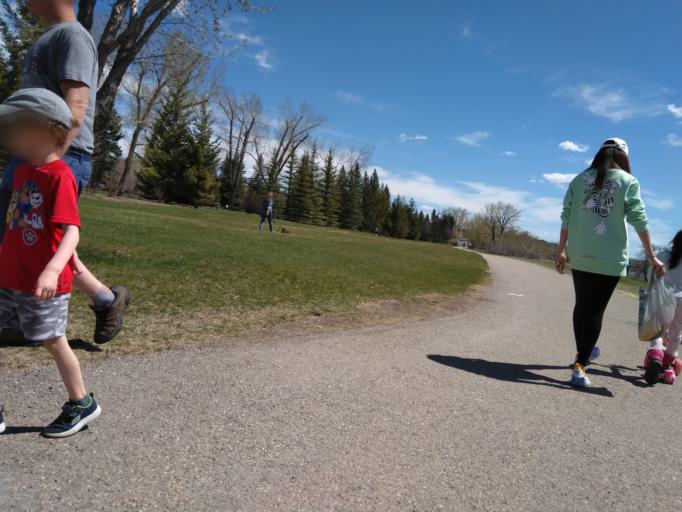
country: CA
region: Alberta
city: Calgary
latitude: 51.0998
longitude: -114.2181
